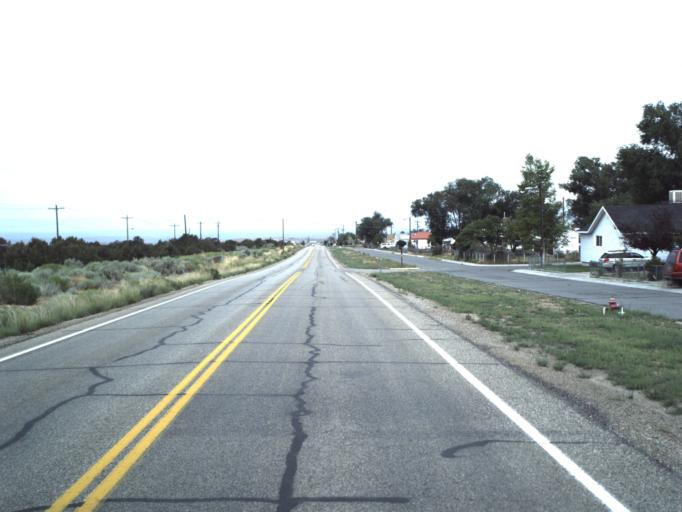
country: US
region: Utah
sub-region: Carbon County
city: East Carbon City
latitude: 39.5444
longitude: -110.4077
